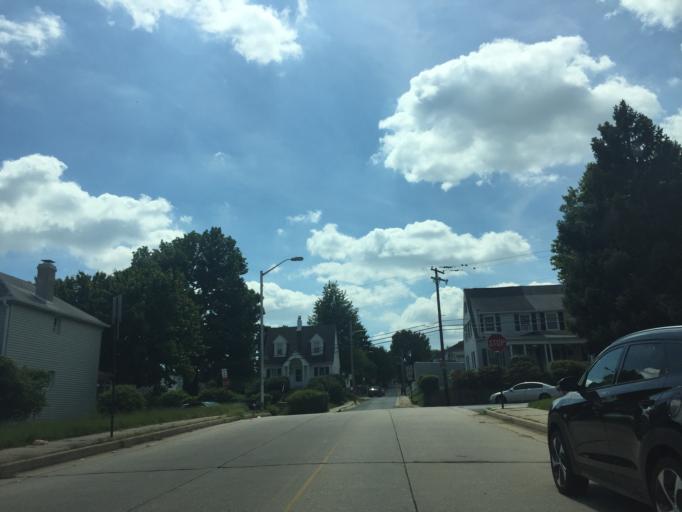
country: US
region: Maryland
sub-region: City of Baltimore
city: Baltimore
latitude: 39.3441
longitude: -76.6423
